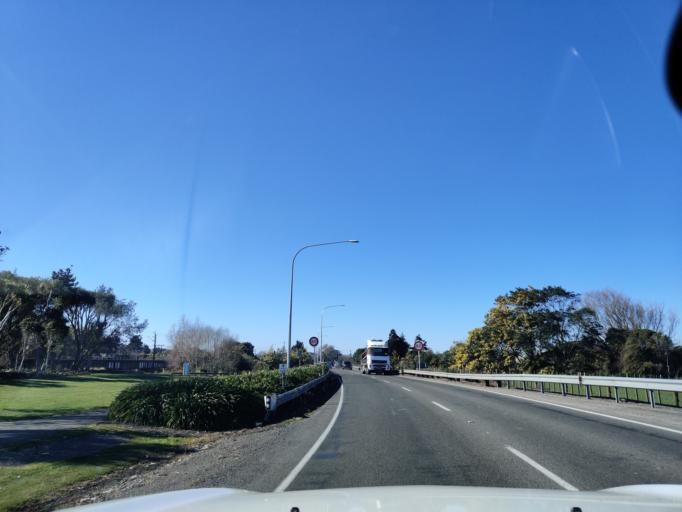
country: NZ
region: Manawatu-Wanganui
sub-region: Palmerston North City
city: Palmerston North
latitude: -40.2377
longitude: 175.5764
